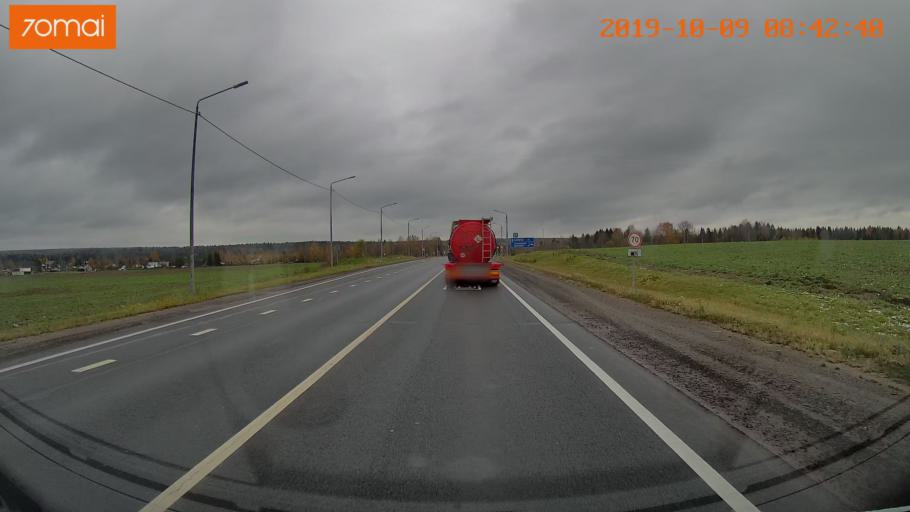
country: RU
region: Vologda
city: Gryazovets
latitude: 59.0179
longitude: 40.1175
